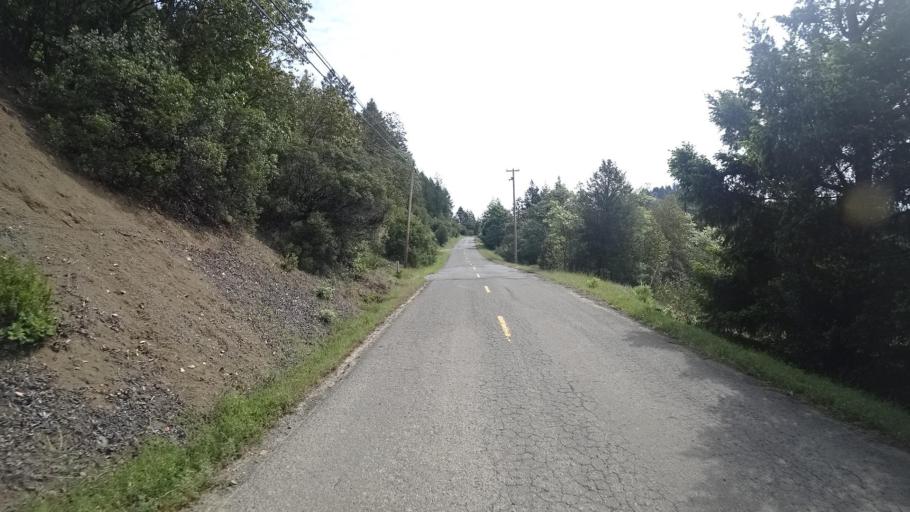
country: US
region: California
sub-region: Humboldt County
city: Redway
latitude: 40.0775
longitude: -123.8240
